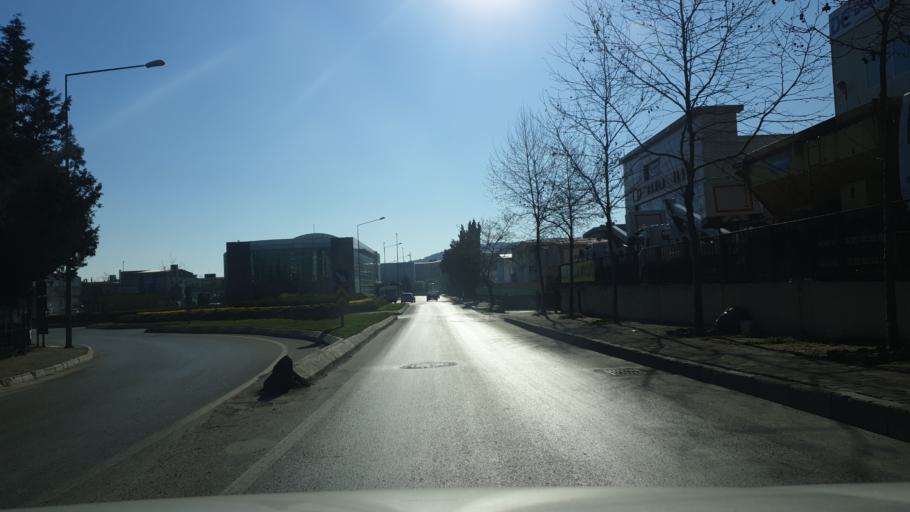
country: TR
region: Kocaeli
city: Balcik
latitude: 40.8791
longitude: 29.3677
